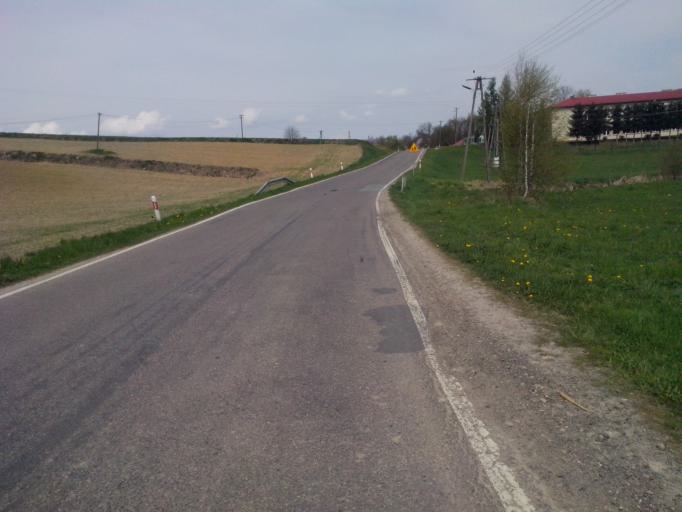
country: PL
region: Subcarpathian Voivodeship
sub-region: Powiat strzyzowski
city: Jawornik
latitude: 49.8131
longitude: 21.8436
